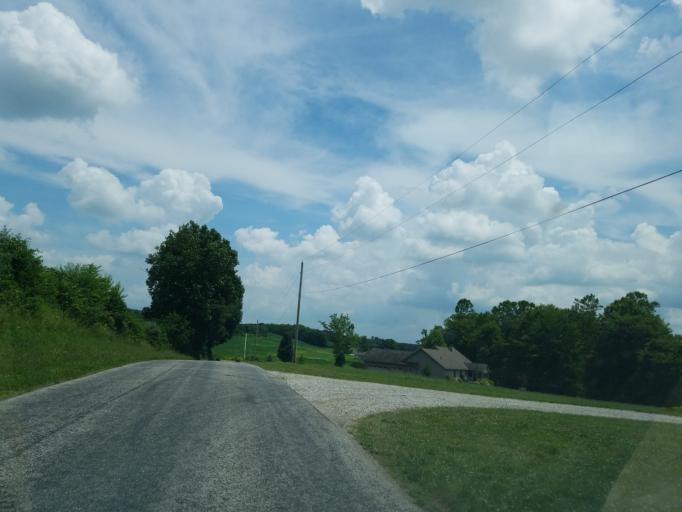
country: US
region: Ohio
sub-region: Licking County
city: Newark
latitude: 40.1315
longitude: -82.4136
